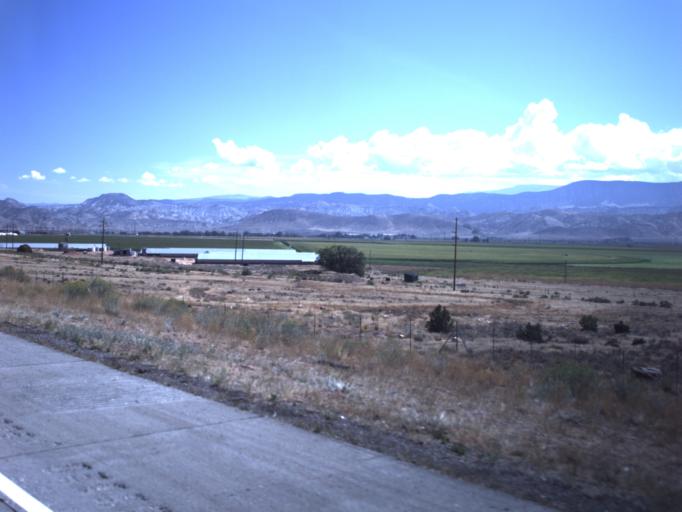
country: US
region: Utah
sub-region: Sevier County
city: Richfield
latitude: 38.8387
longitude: -112.0248
